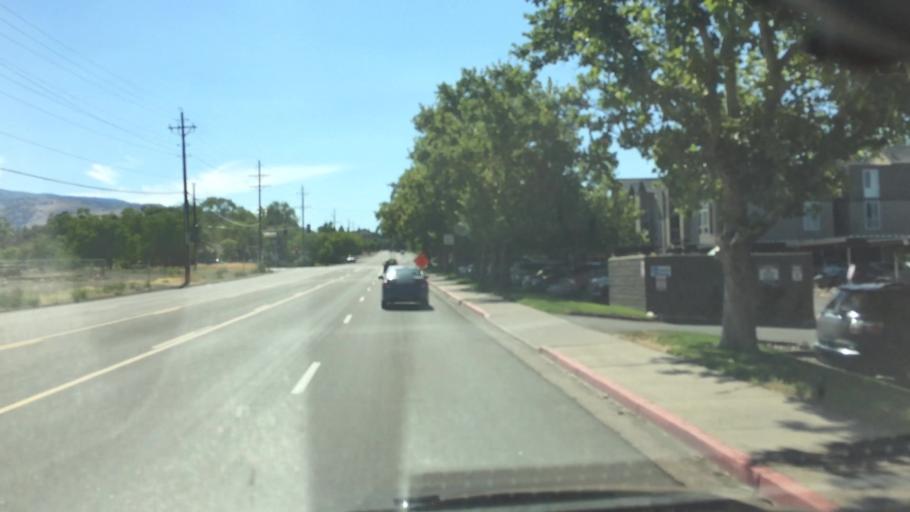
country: US
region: Nevada
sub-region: Washoe County
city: Reno
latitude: 39.4913
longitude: -119.8108
